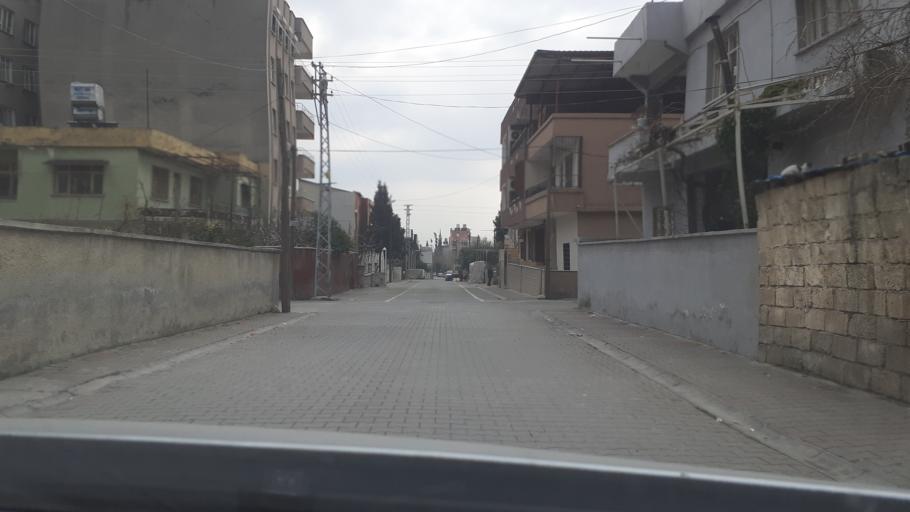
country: TR
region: Hatay
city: Kirikhan
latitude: 36.4939
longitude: 36.3524
